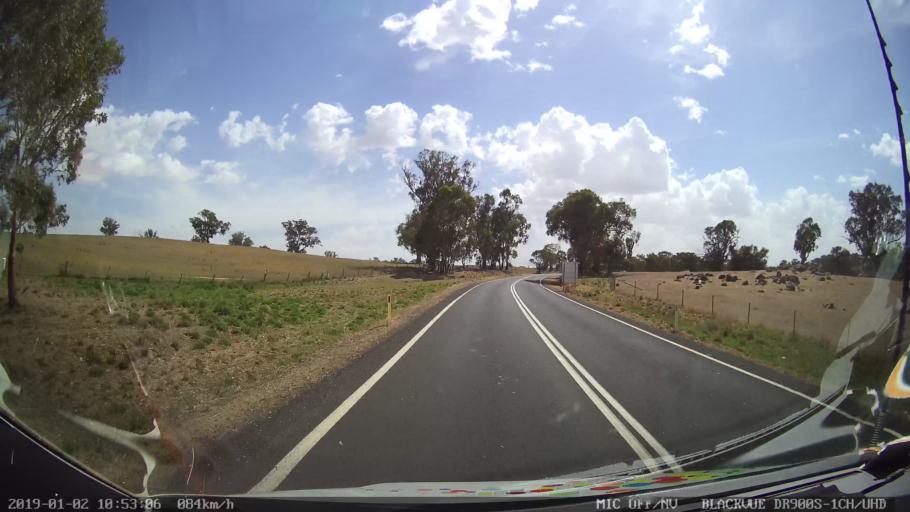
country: AU
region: New South Wales
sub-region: Cootamundra
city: Cootamundra
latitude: -34.6810
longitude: 148.2722
